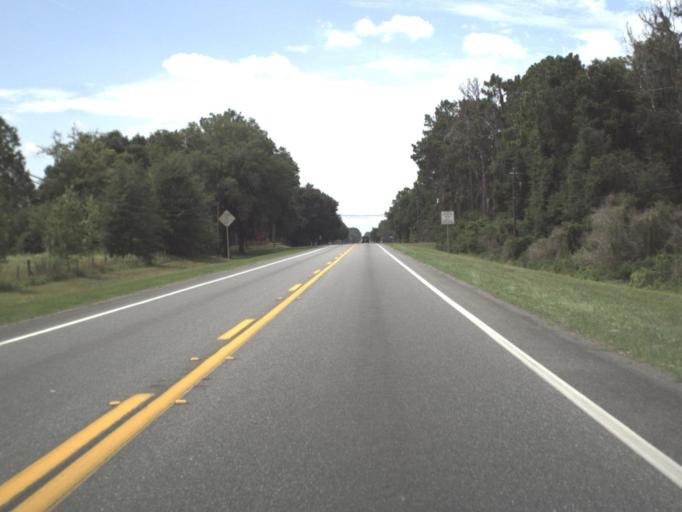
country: US
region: Florida
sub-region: Suwannee County
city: Live Oak
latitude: 30.2731
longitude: -82.9878
